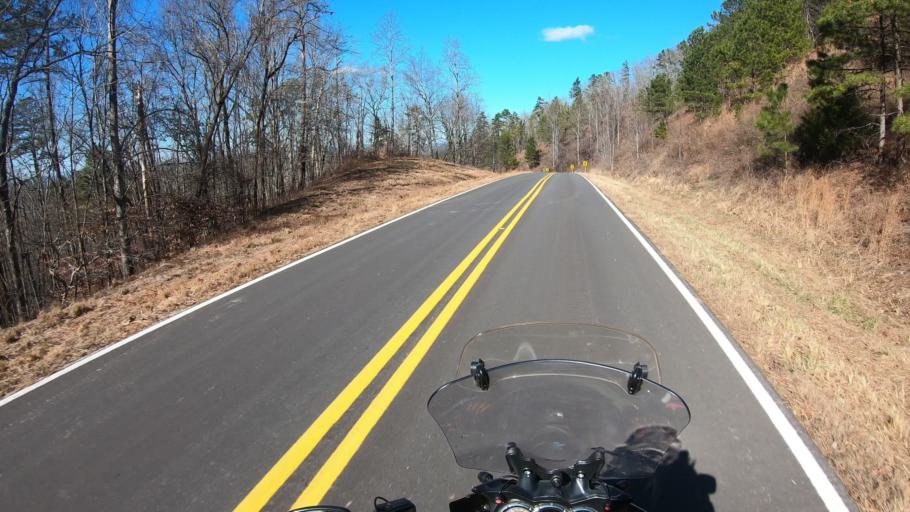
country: US
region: Alabama
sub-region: Clay County
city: Ashland
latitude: 33.4063
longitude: -85.8744
